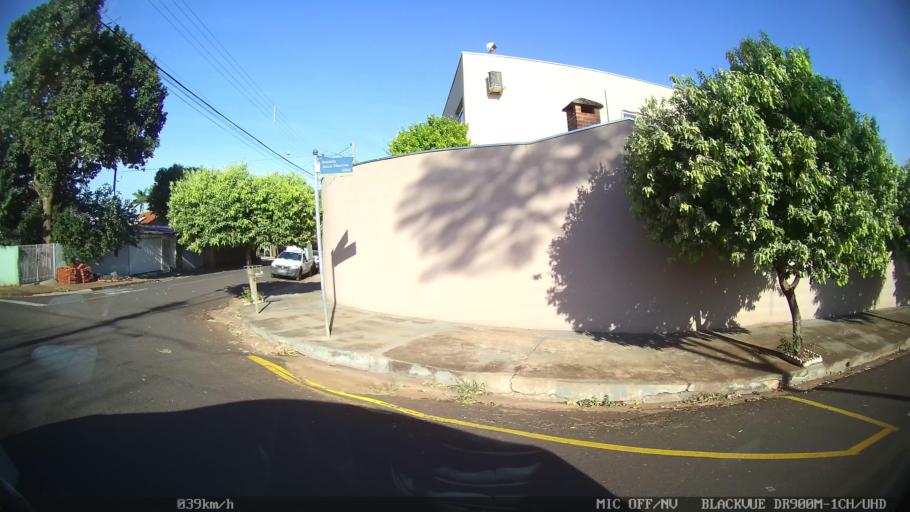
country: BR
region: Sao Paulo
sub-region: Sao Jose Do Rio Preto
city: Sao Jose do Rio Preto
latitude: -20.8211
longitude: -49.4104
